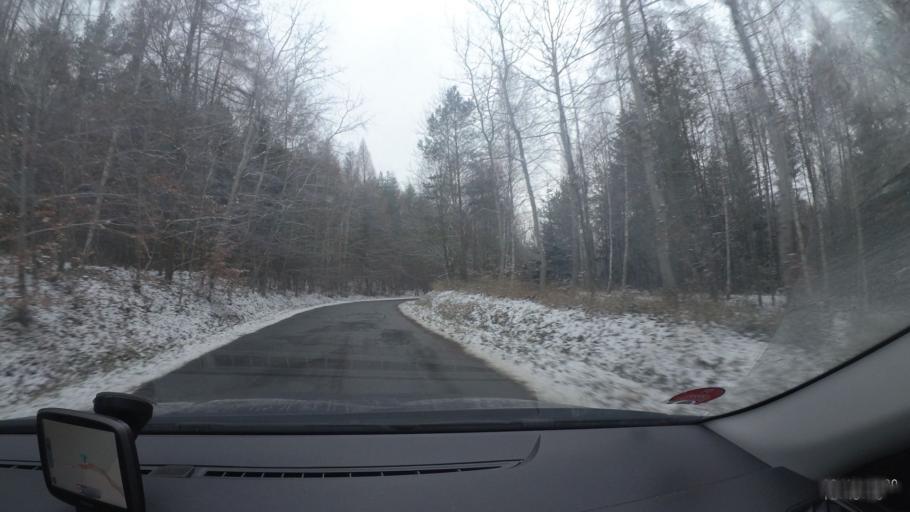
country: CZ
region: Central Bohemia
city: Nove Straseci
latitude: 50.1673
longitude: 13.8700
